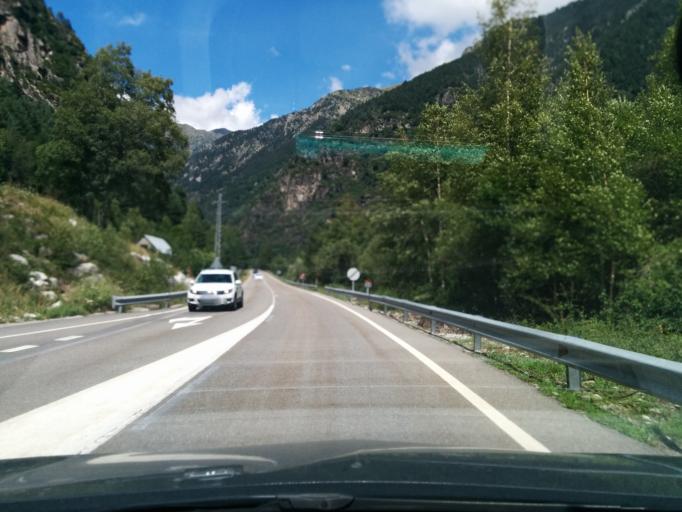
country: ES
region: Aragon
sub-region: Provincia de Huesca
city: Bielsa
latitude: 42.6653
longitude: 0.2121
